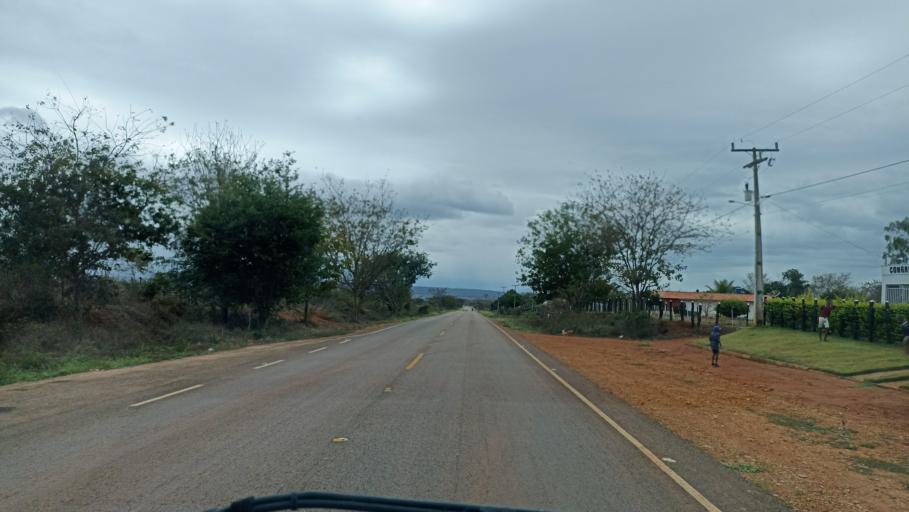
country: BR
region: Bahia
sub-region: Andarai
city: Vera Cruz
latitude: -12.9679
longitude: -41.0307
